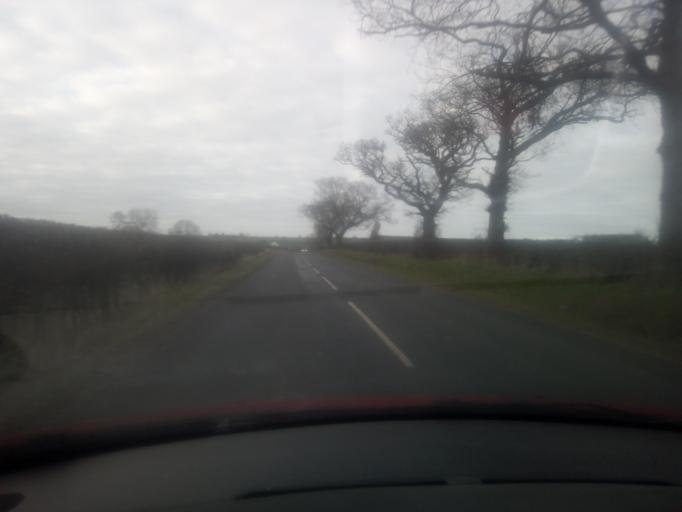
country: GB
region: England
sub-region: Darlington
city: Summerhouse
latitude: 54.5810
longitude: -1.6785
